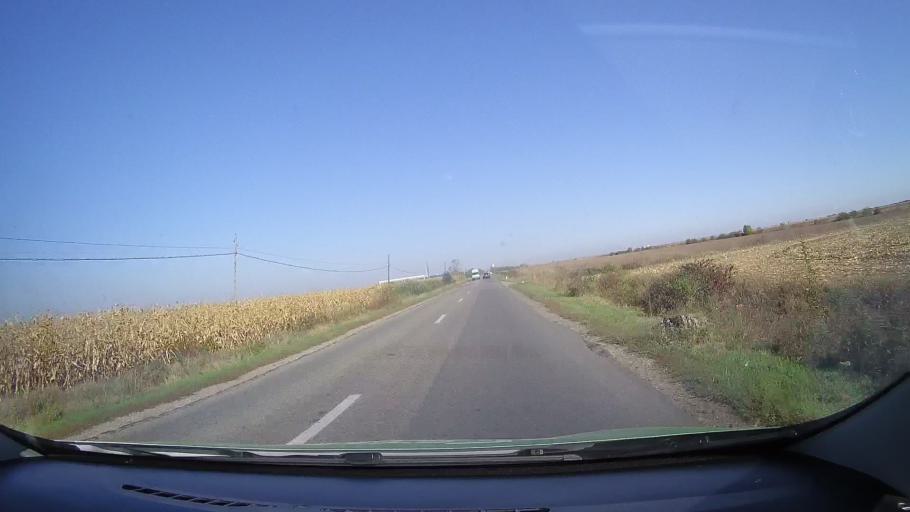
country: RO
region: Satu Mare
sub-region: Oras Tasnad
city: Tasnad
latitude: 47.4999
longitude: 22.5747
